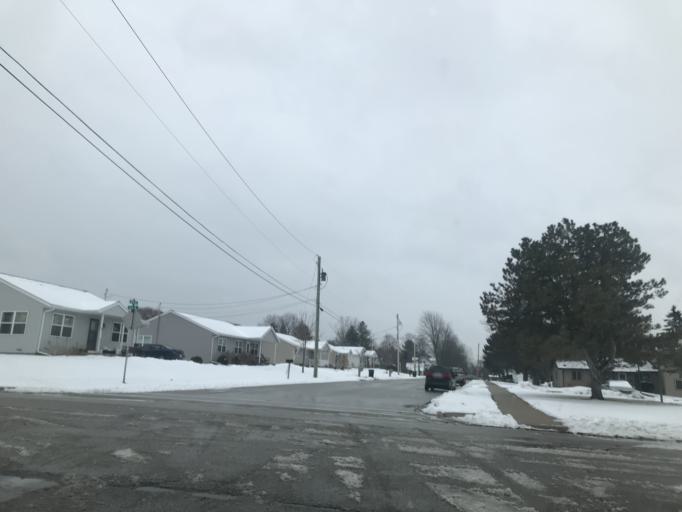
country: US
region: Wisconsin
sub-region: Door County
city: Sturgeon Bay
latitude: 44.8444
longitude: -87.3743
